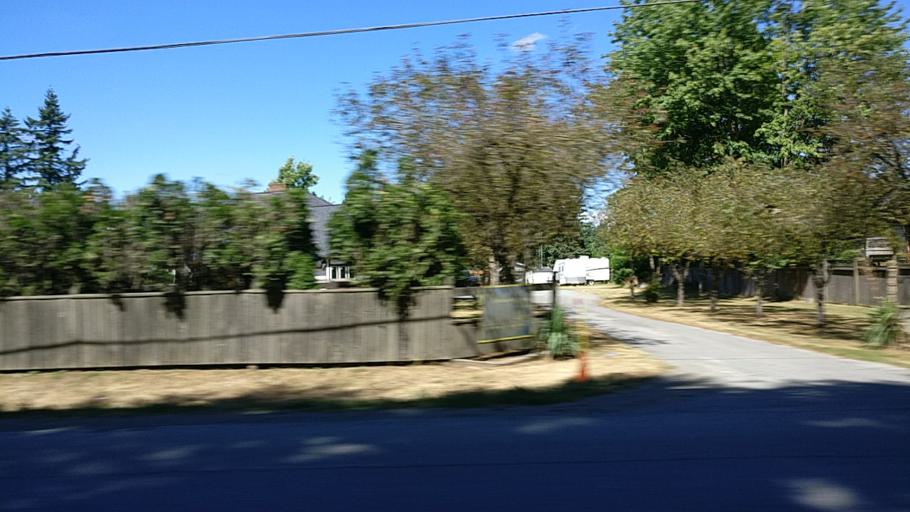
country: CA
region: British Columbia
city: Aldergrove
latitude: 49.0315
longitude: -122.4626
